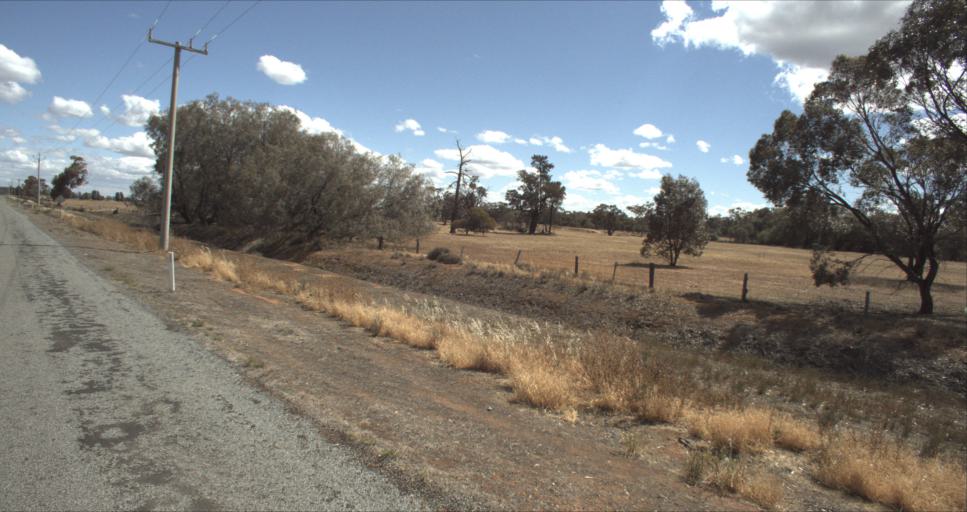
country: AU
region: New South Wales
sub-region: Leeton
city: Leeton
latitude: -34.5189
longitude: 146.2252
